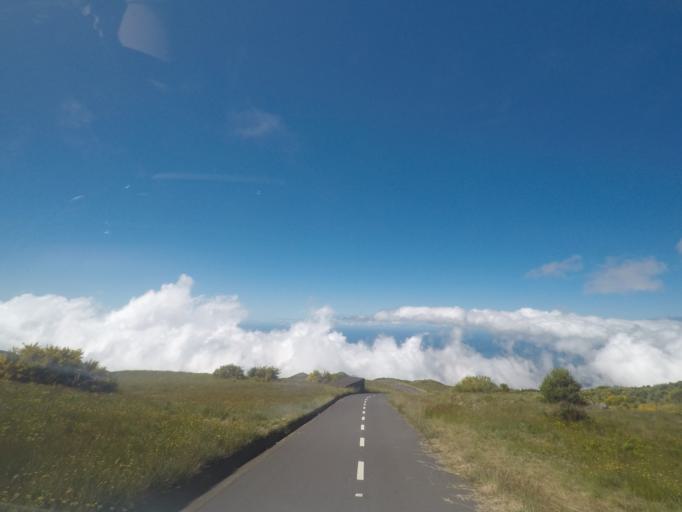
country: PT
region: Madeira
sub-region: Camara de Lobos
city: Curral das Freiras
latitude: 32.7139
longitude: -16.9382
